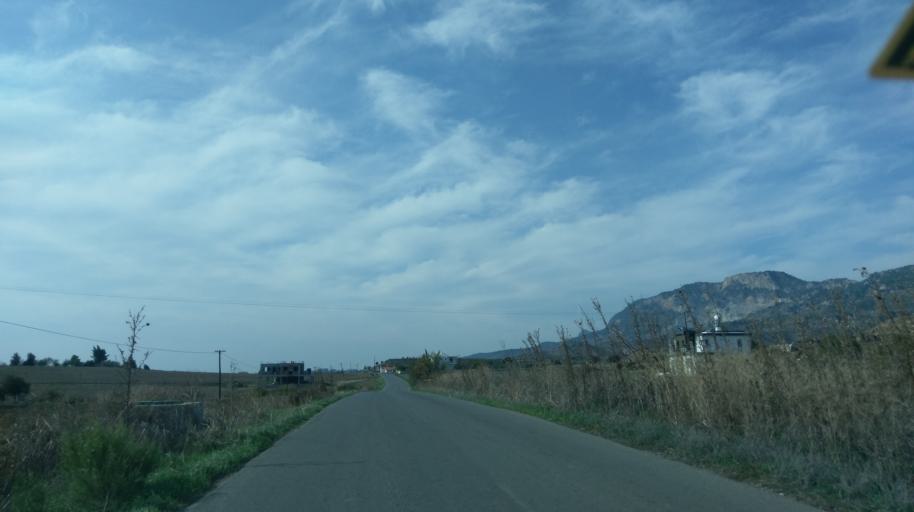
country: CY
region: Keryneia
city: Lapithos
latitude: 35.2822
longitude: 33.2210
